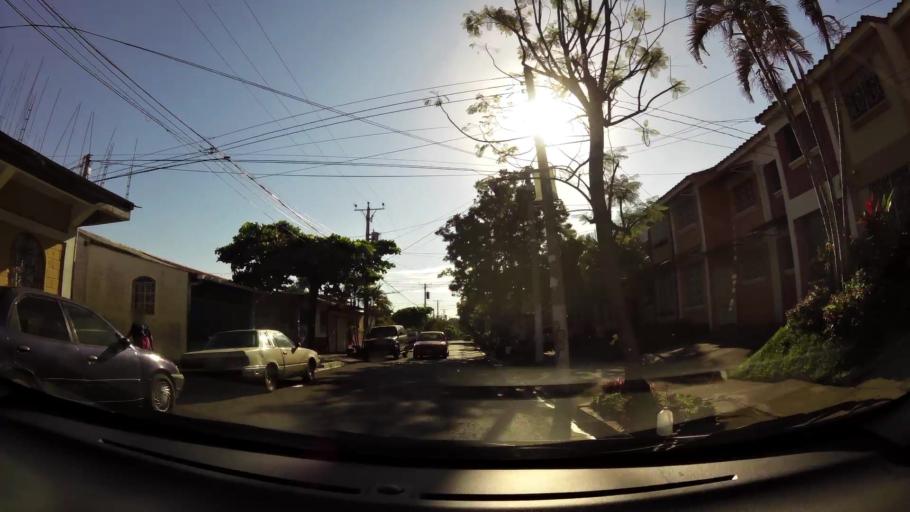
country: SV
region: Sonsonate
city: Sonzacate
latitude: 13.7295
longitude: -89.7128
